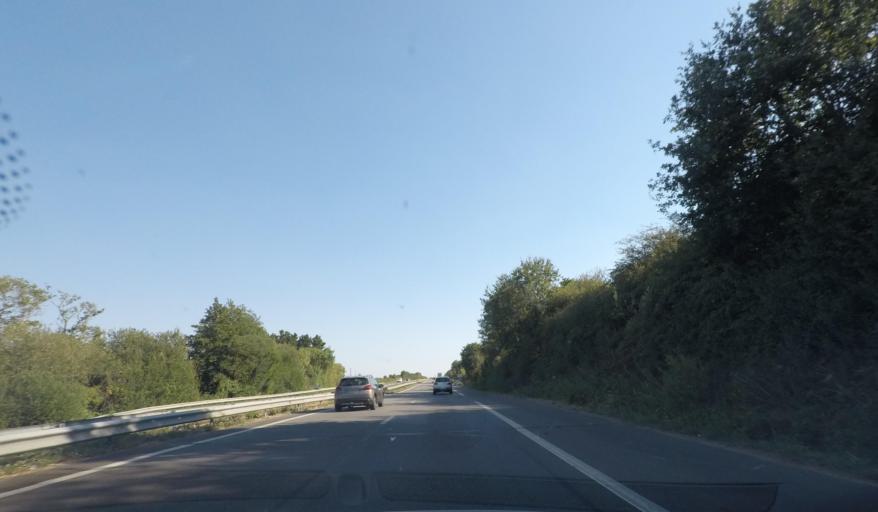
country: FR
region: Pays de la Loire
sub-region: Departement de la Loire-Atlantique
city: Saint-Brevin-les-Pins
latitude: 47.2234
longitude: -2.1525
